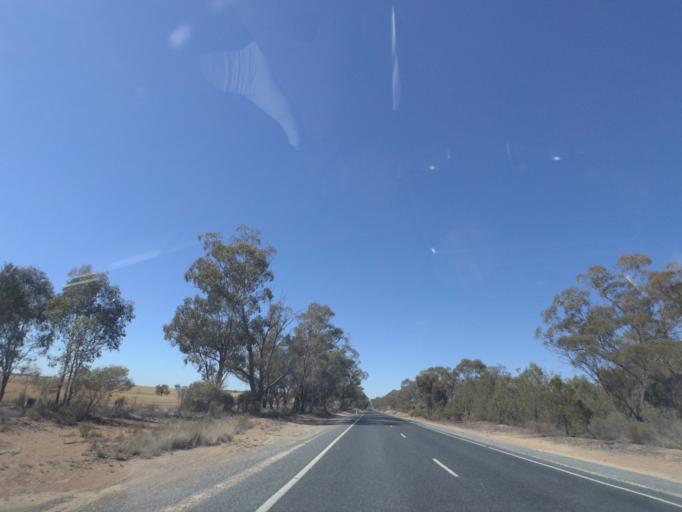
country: AU
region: New South Wales
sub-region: Bland
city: West Wyalong
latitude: -34.1431
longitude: 147.1198
